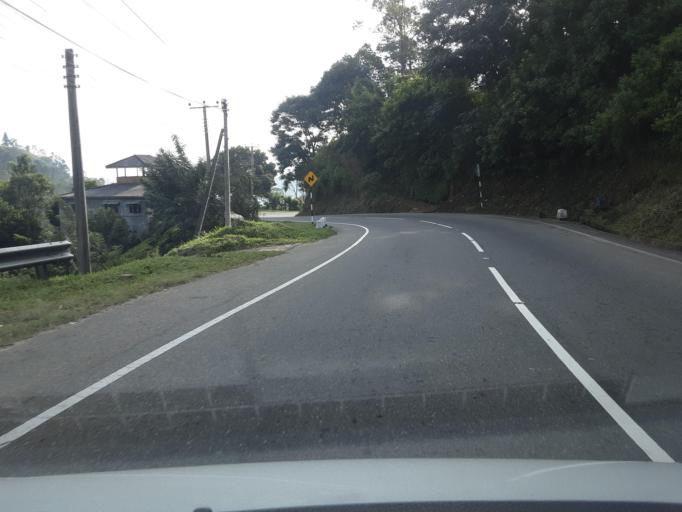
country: LK
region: Uva
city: Badulla
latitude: 6.9392
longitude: 80.9999
